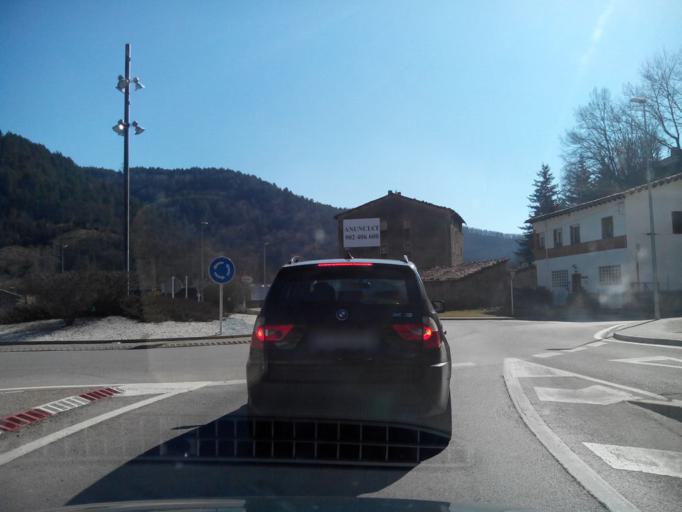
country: ES
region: Catalonia
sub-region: Provincia de Girona
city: Ripoll
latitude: 42.1874
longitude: 2.1964
